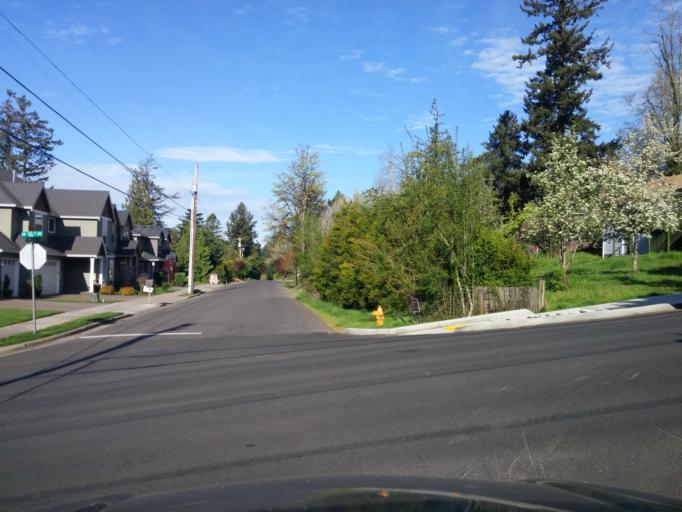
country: US
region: Oregon
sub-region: Washington County
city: Cedar Mill
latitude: 45.5332
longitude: -122.7926
